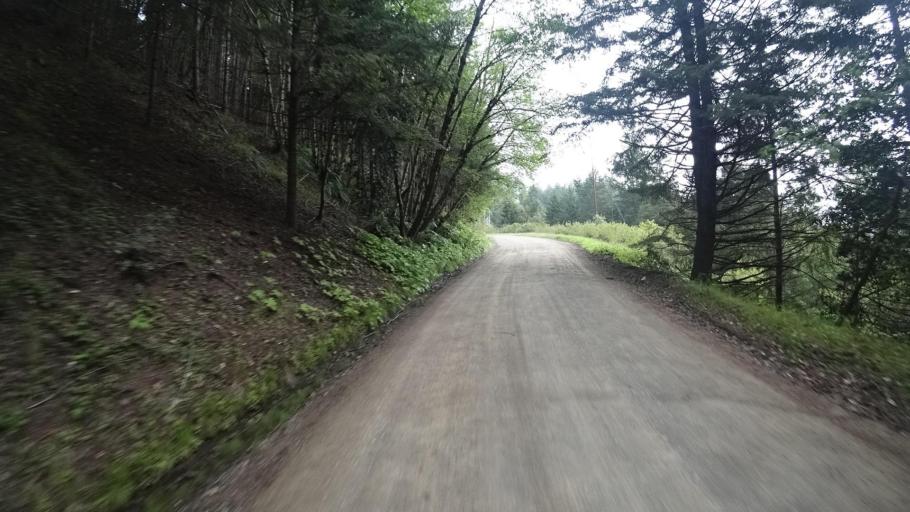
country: US
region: California
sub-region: Humboldt County
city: Redway
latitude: 40.2633
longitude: -123.7698
